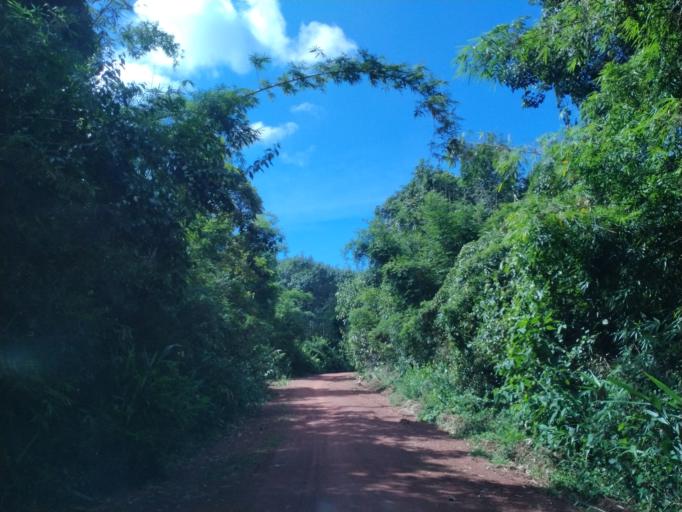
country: LA
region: Vientiane
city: Muang Phon-Hong
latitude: 18.6444
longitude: 102.8966
